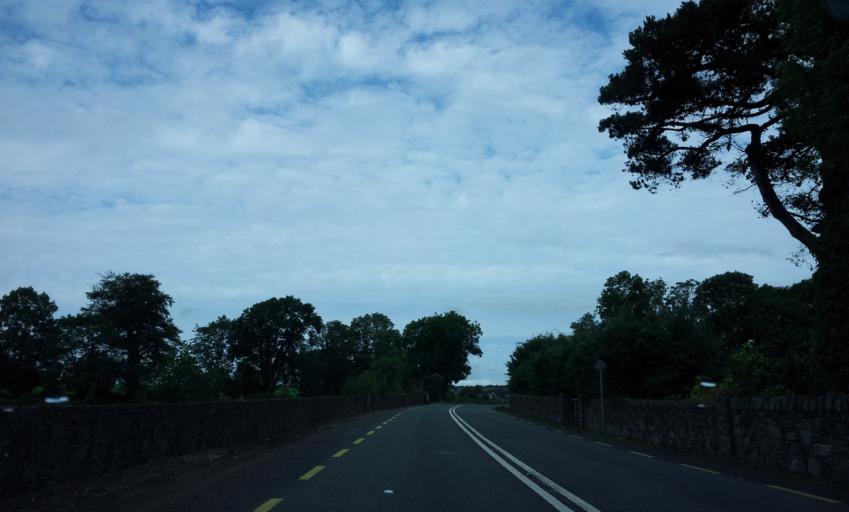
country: IE
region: Munster
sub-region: Ciarrai
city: Cill Airne
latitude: 52.0723
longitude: -9.6116
